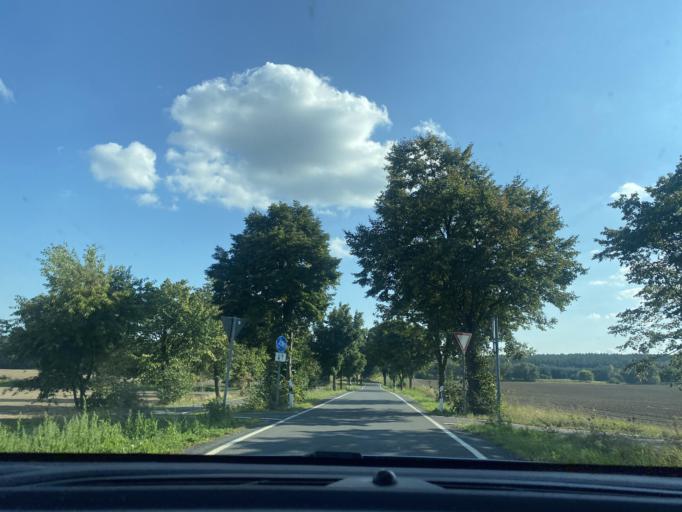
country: DE
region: Saxony
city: Quitzdorf
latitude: 51.2618
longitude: 14.7356
